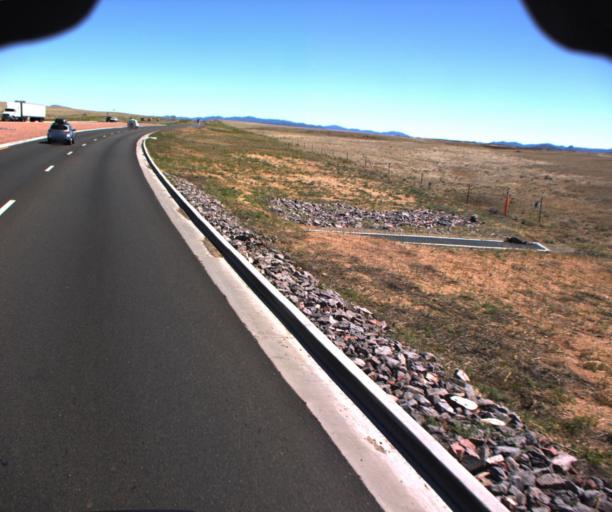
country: US
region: Arizona
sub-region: Yavapai County
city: Chino Valley
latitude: 34.7047
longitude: -112.4506
